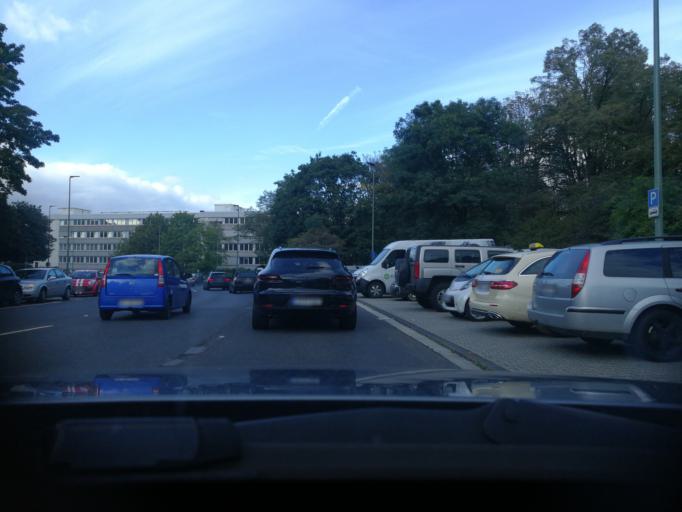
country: DE
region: North Rhine-Westphalia
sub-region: Regierungsbezirk Dusseldorf
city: Neuss
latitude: 51.2025
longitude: 6.7239
